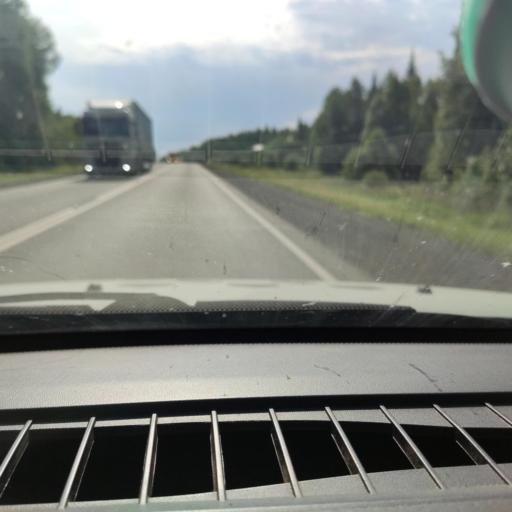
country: RU
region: Perm
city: Zyukayka
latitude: 58.3766
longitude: 54.6274
